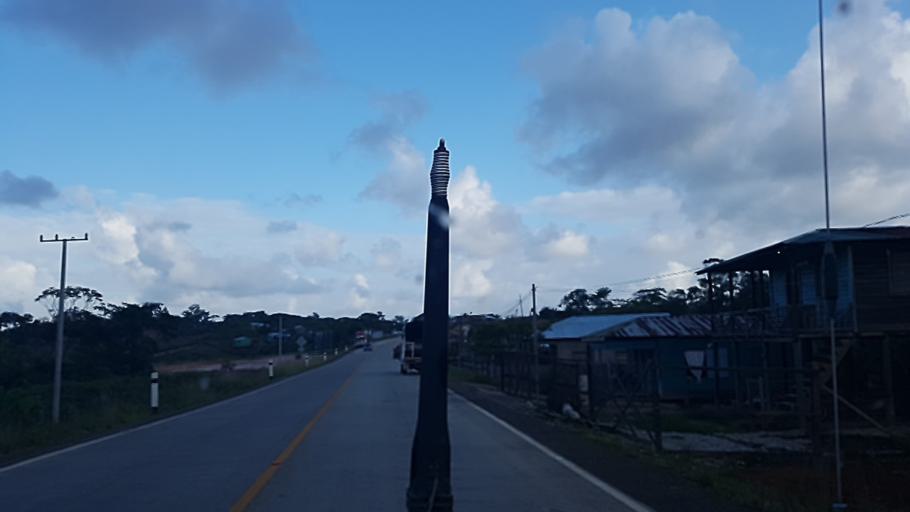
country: NI
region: Atlantico Sur
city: Bluefields
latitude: 12.0052
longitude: -83.7869
